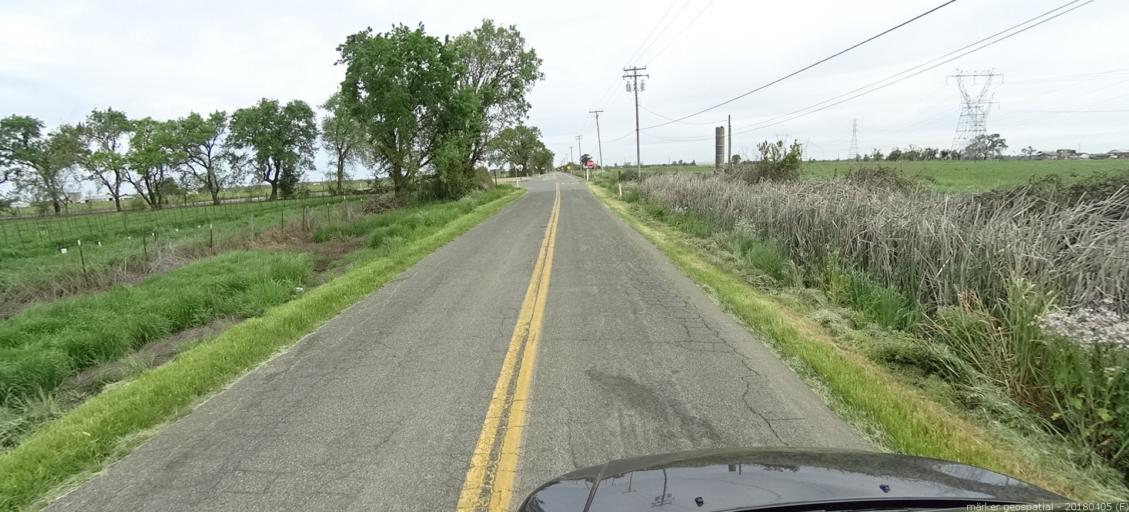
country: US
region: California
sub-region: San Joaquin County
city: Thornton
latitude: 38.2421
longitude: -121.3692
